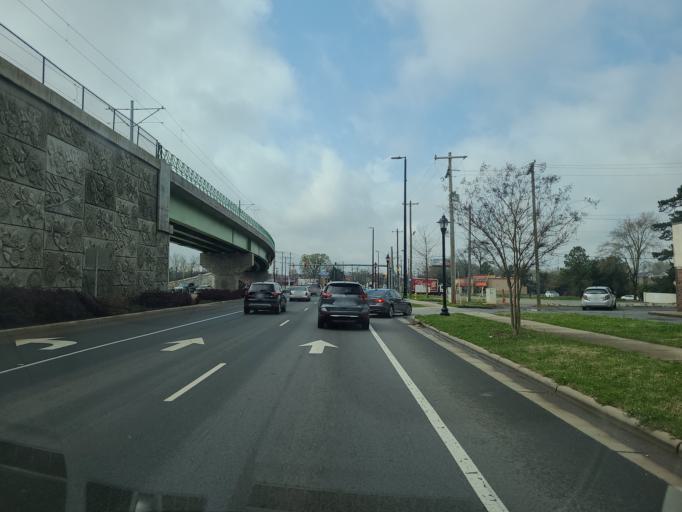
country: US
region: North Carolina
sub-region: Mecklenburg County
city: Charlotte
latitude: 35.2637
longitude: -80.7714
